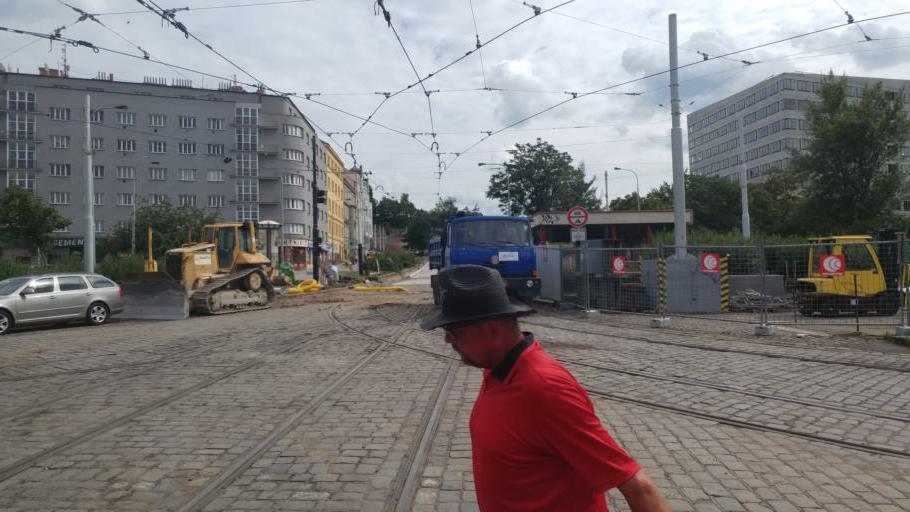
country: CZ
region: Praha
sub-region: Praha 8
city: Liben
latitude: 50.1035
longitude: 14.4736
